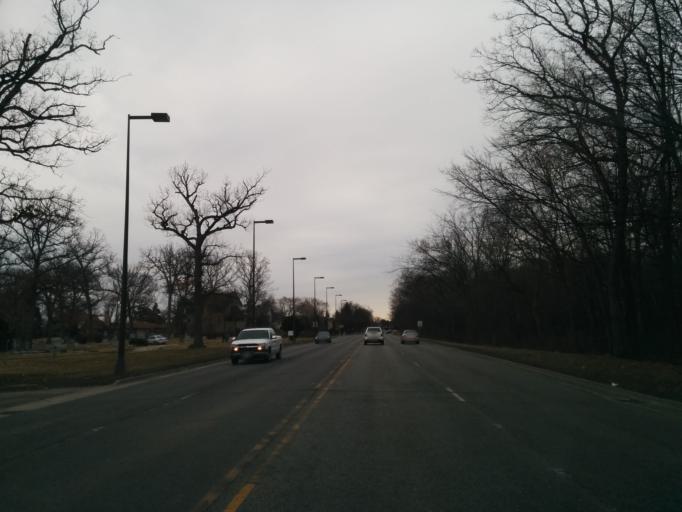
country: US
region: Illinois
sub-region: Cook County
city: Westchester
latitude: 41.8394
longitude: -87.8766
